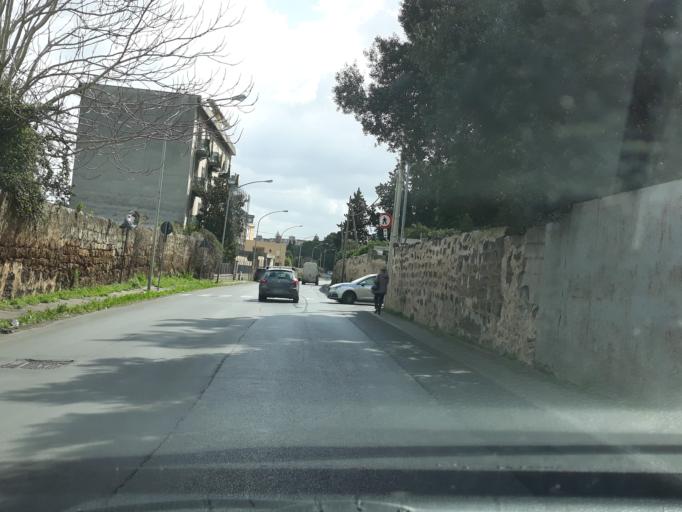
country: IT
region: Sicily
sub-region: Palermo
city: Palermo
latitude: 38.1251
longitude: 13.3157
